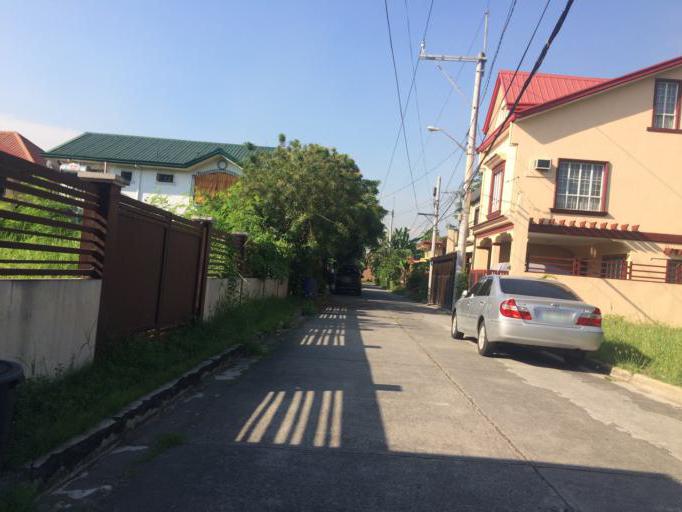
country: PH
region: Calabarzon
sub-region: Province of Rizal
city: Taytay
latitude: 14.5518
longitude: 121.1080
